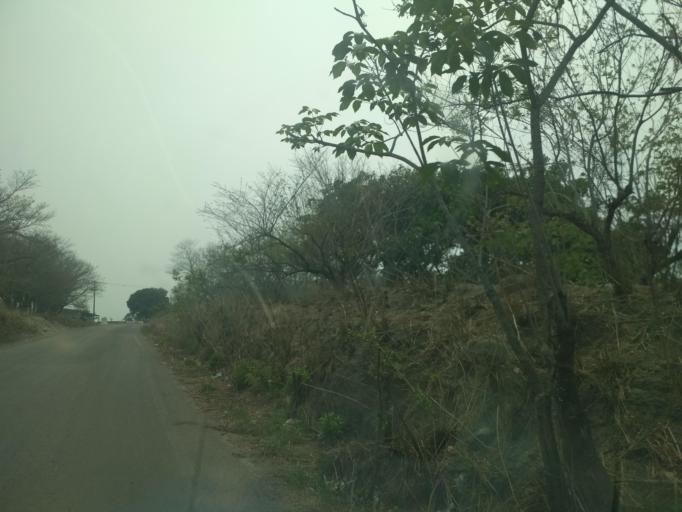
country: MX
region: Veracruz
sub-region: Veracruz
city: Delfino Victoria (Santa Fe)
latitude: 19.1889
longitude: -96.3095
